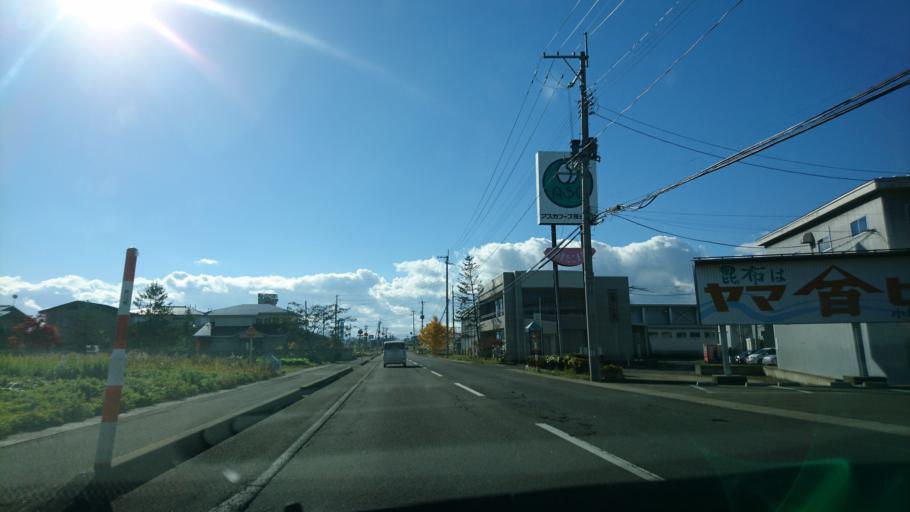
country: JP
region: Akita
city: Yokotemachi
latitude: 39.2713
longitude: 140.4979
